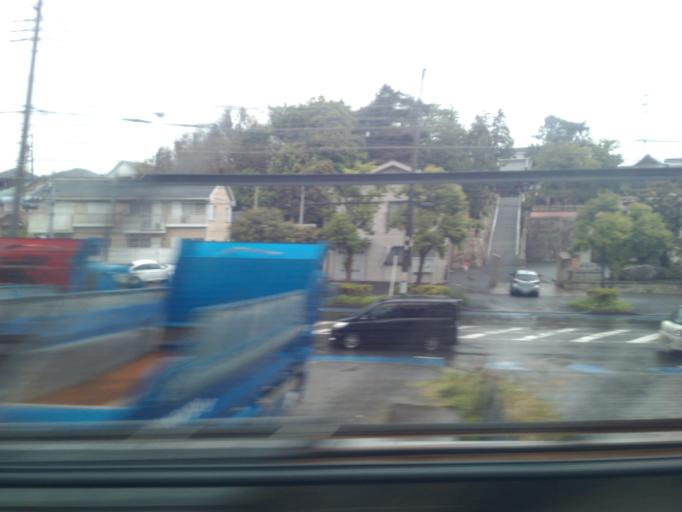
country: JP
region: Kanagawa
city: Minami-rinkan
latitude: 35.4494
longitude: 139.5107
